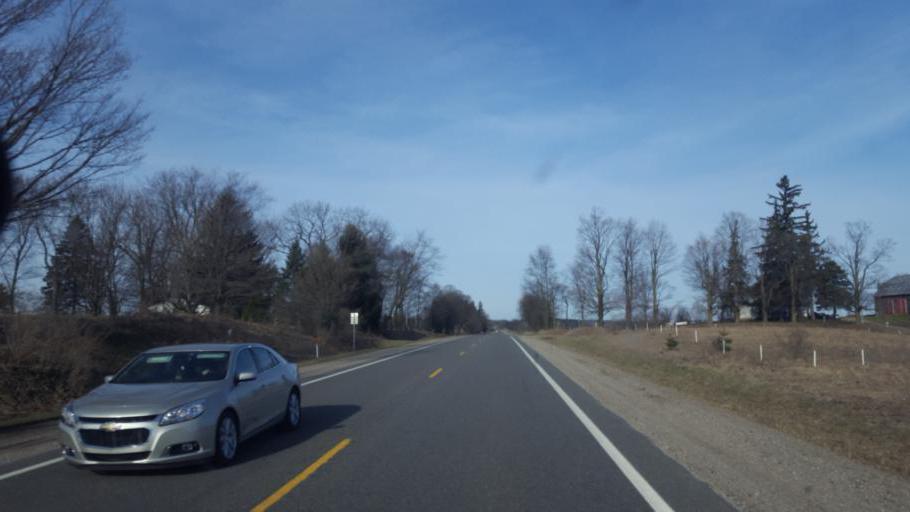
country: US
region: Michigan
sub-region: Montcalm County
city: Lakeview
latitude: 43.4315
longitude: -85.3115
